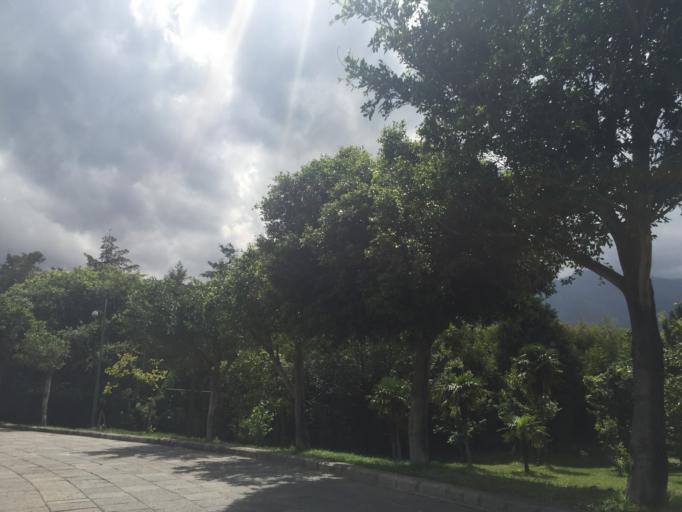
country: CN
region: Yunnan
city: Dali
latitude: 25.7074
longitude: 100.1408
